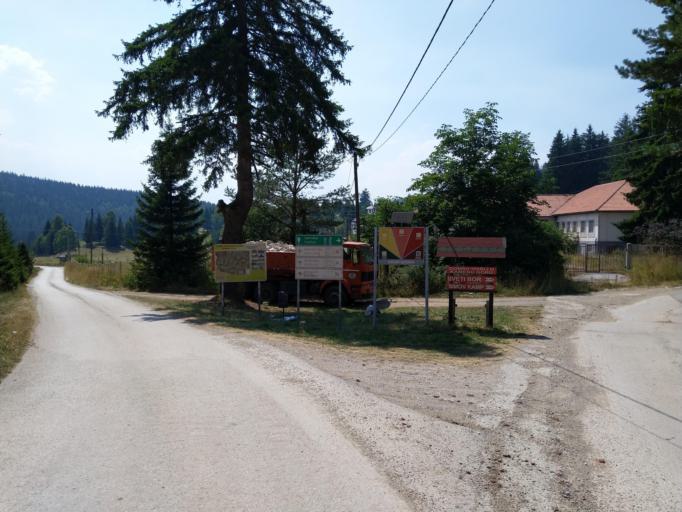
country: RS
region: Central Serbia
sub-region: Zlatiborski Okrug
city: Prijepolje
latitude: 43.2829
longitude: 19.5641
